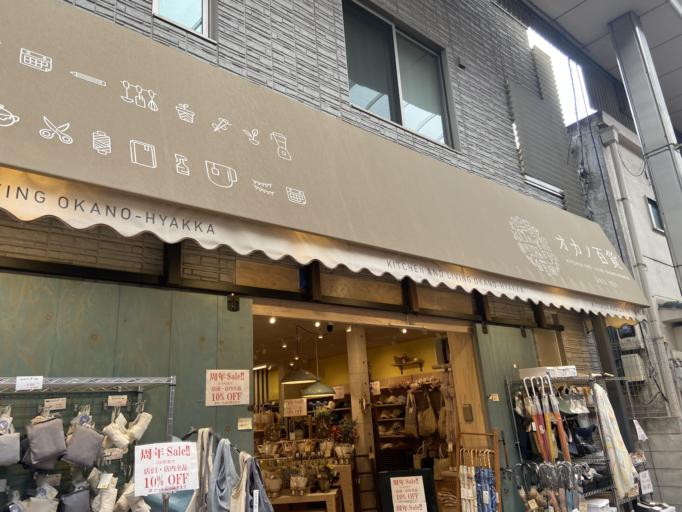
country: JP
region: Osaka
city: Osaka-shi
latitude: 34.7116
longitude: 135.4669
